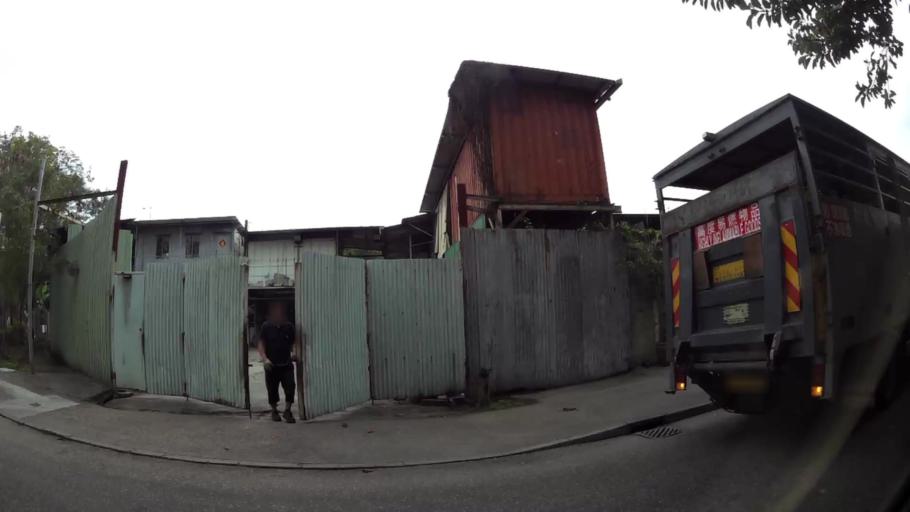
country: HK
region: Tuen Mun
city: Tuen Mun
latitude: 22.4232
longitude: 113.9938
